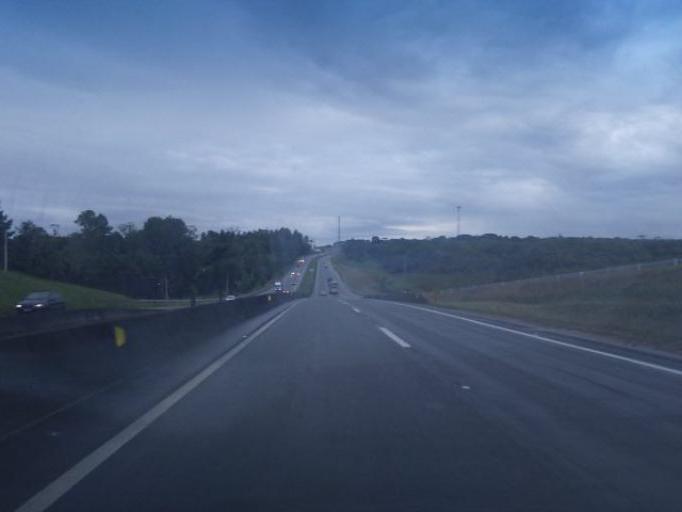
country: BR
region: Parana
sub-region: Sao Jose Dos Pinhais
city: Sao Jose dos Pinhais
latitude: -25.7699
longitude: -49.1229
